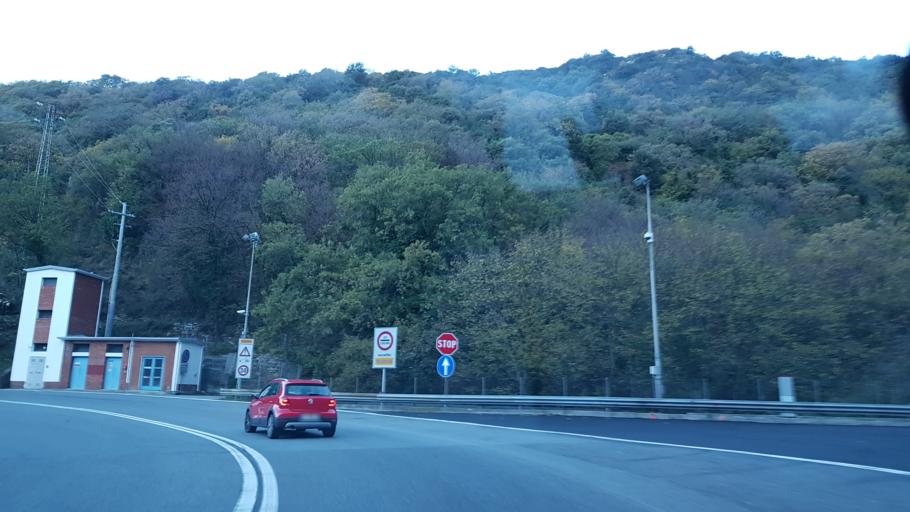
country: IT
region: Liguria
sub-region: Provincia di Genova
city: Bogliasco
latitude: 44.3981
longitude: 9.0152
